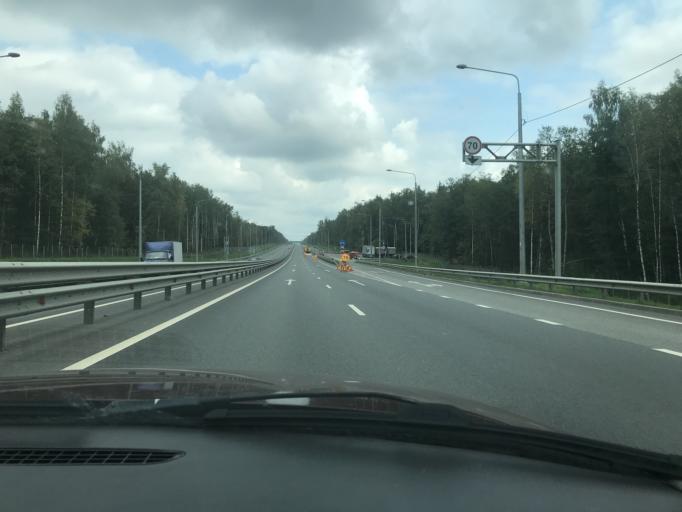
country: RU
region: Kaluga
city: Mstikhino
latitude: 54.5943
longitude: 36.0853
